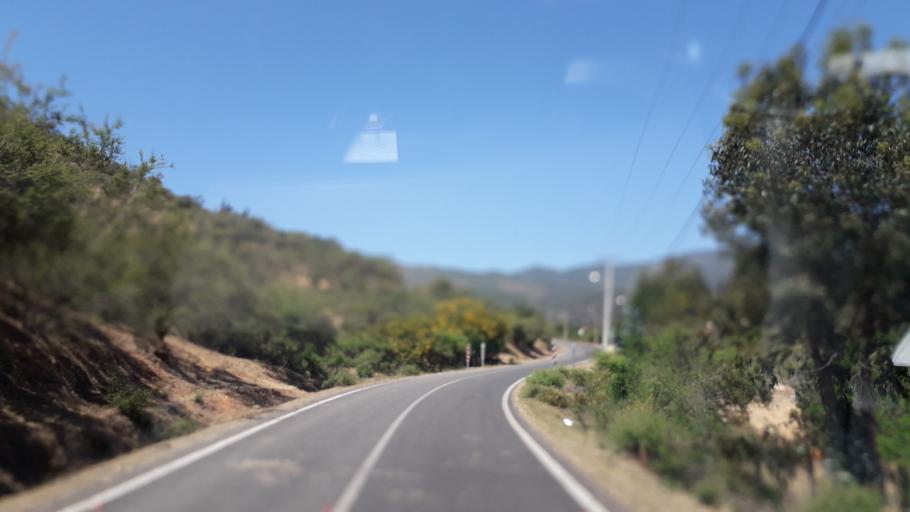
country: CL
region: Valparaiso
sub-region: Provincia de Marga Marga
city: Limache
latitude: -33.0906
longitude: -71.2127
